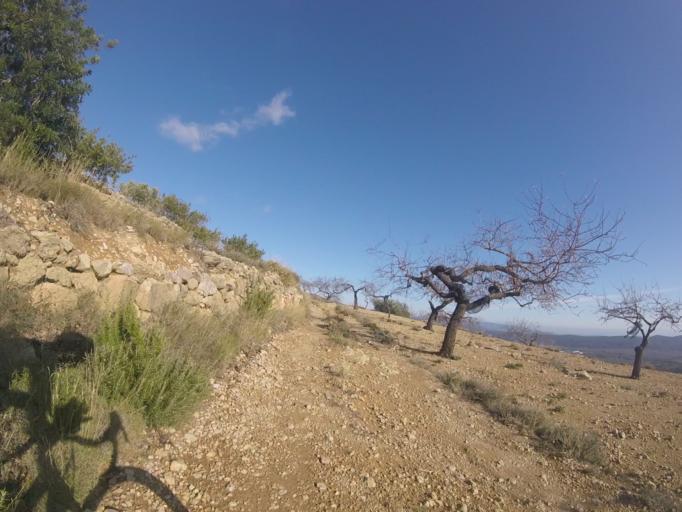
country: ES
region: Valencia
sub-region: Provincia de Castello
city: Sarratella
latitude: 40.2969
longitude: 0.0459
